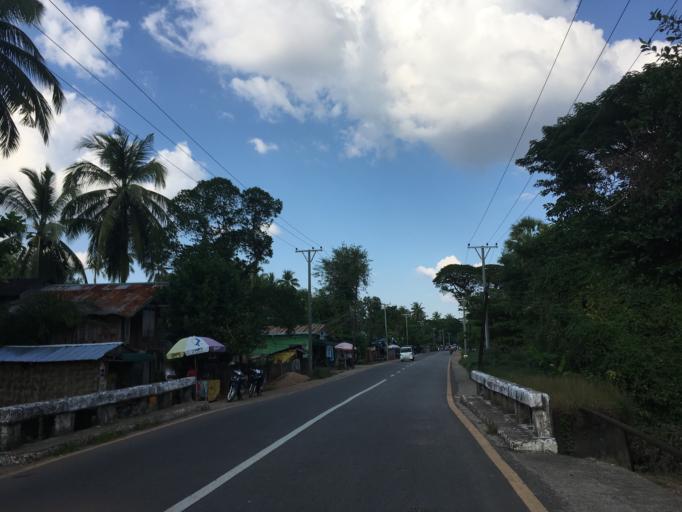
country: MM
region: Mon
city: Mawlamyine
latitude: 16.4440
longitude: 97.6189
